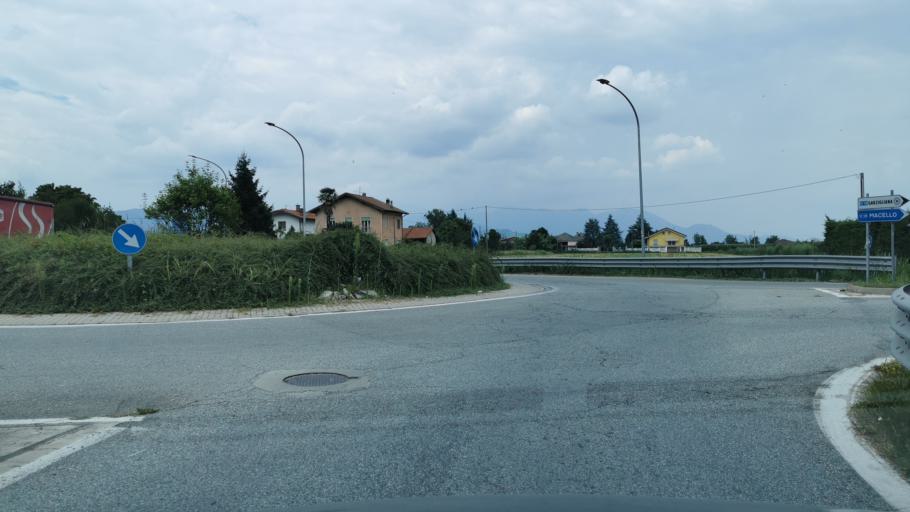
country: IT
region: Piedmont
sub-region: Provincia di Torino
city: Osasco
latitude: 44.8406
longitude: 7.3546
